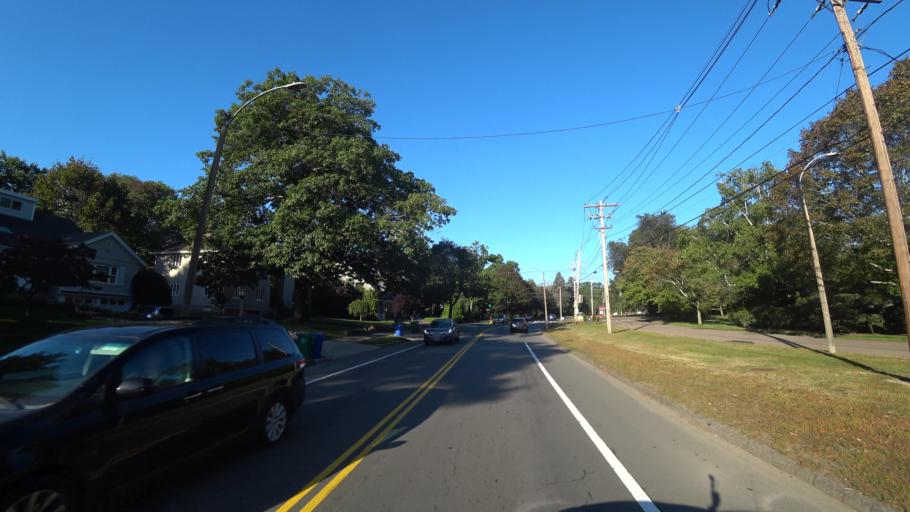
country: US
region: Massachusetts
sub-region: Middlesex County
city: Newton
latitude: 42.3367
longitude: -71.2226
